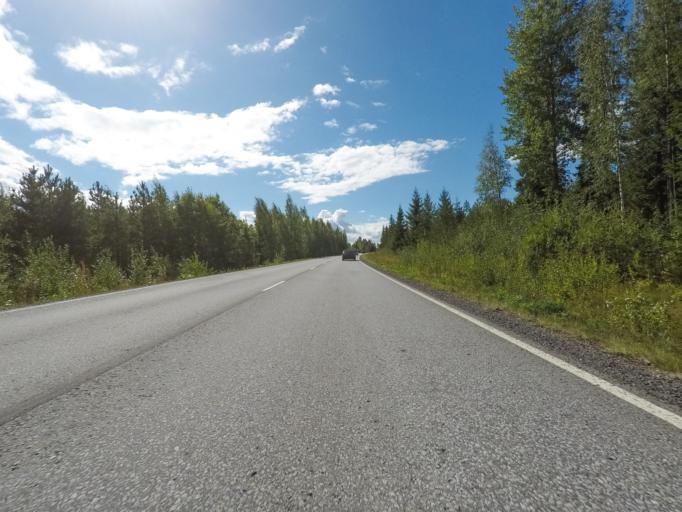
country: FI
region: Central Finland
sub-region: Jyvaeskylae
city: Toivakka
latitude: 62.1890
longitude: 26.1998
